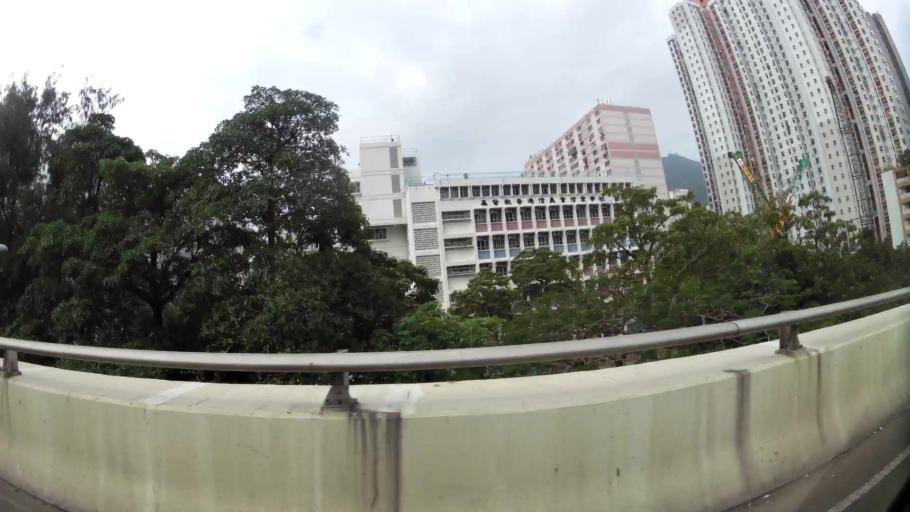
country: HK
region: Wanchai
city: Wan Chai
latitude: 22.2668
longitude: 114.2427
